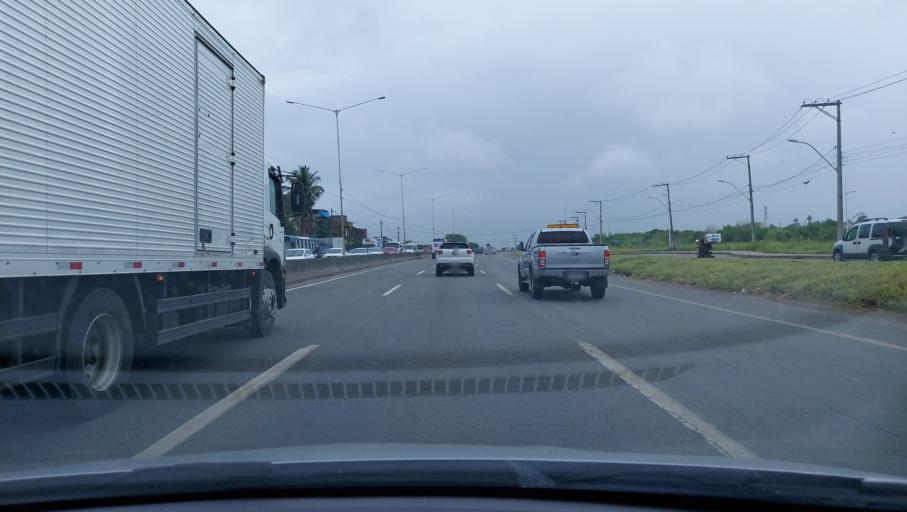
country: BR
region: Bahia
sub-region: Salvador
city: Salvador
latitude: -12.8924
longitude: -38.4462
